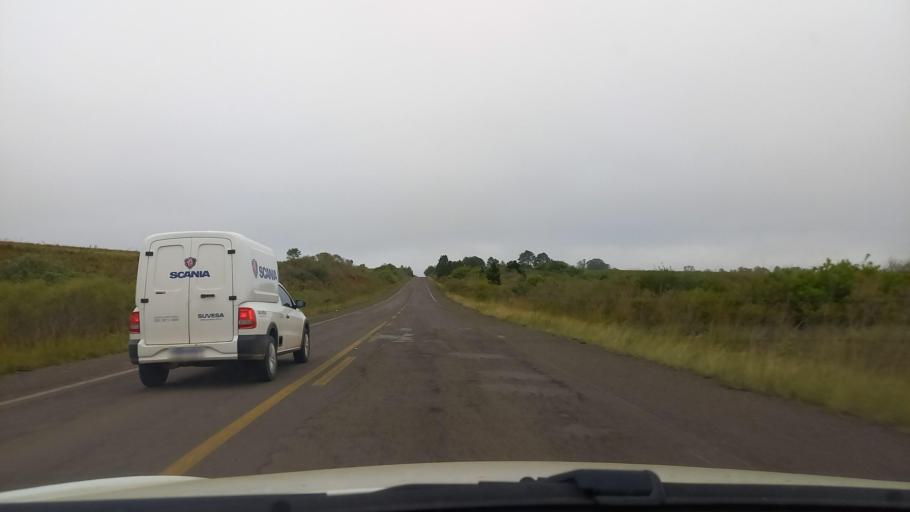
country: BR
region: Rio Grande do Sul
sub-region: Cacequi
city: Cacequi
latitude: -30.0819
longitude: -54.6203
